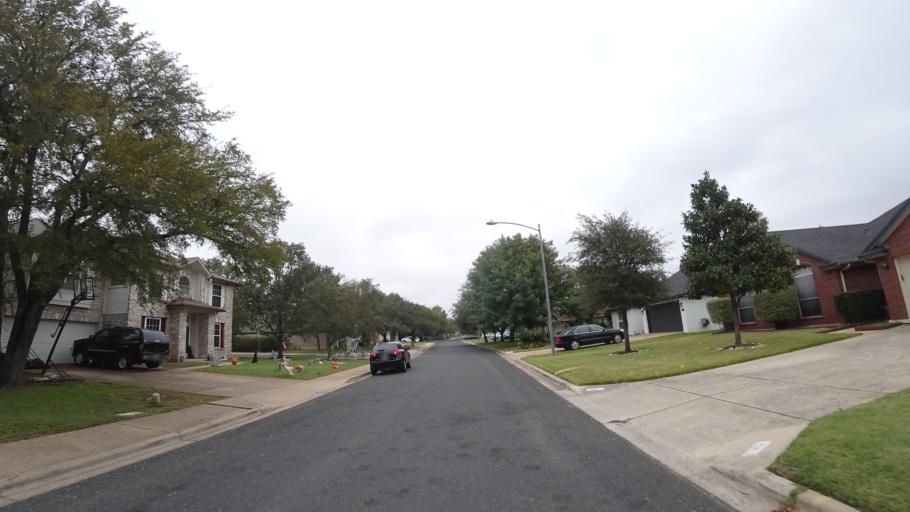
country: US
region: Texas
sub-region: Travis County
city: Shady Hollow
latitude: 30.1873
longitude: -97.8403
